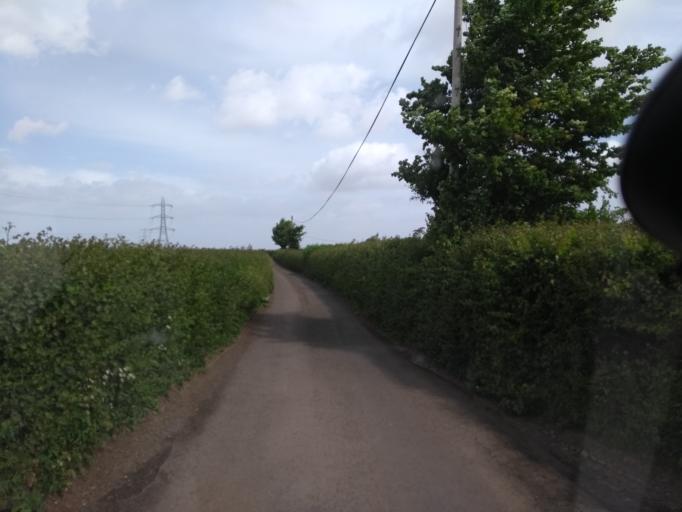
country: GB
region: England
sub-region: Somerset
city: Bridgwater
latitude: 51.1798
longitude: -3.0943
